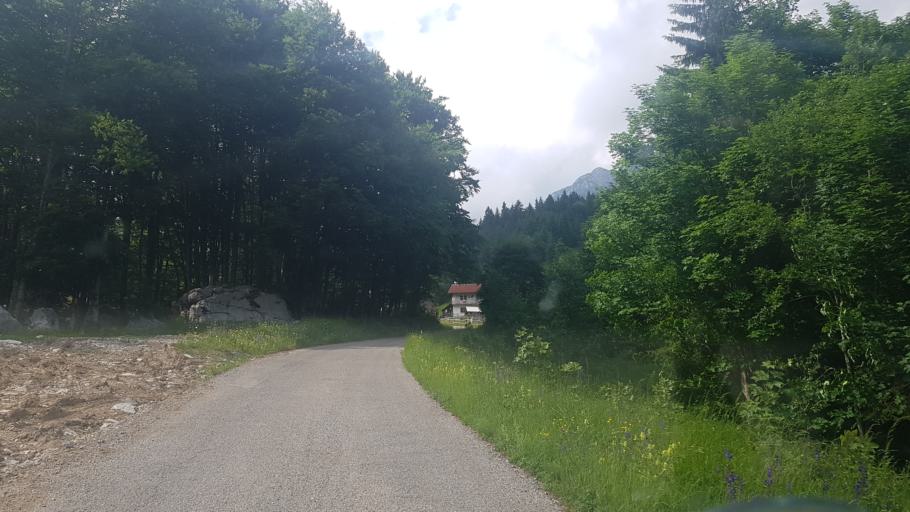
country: IT
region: Friuli Venezia Giulia
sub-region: Provincia di Udine
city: Paularo
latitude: 46.5309
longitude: 13.2107
